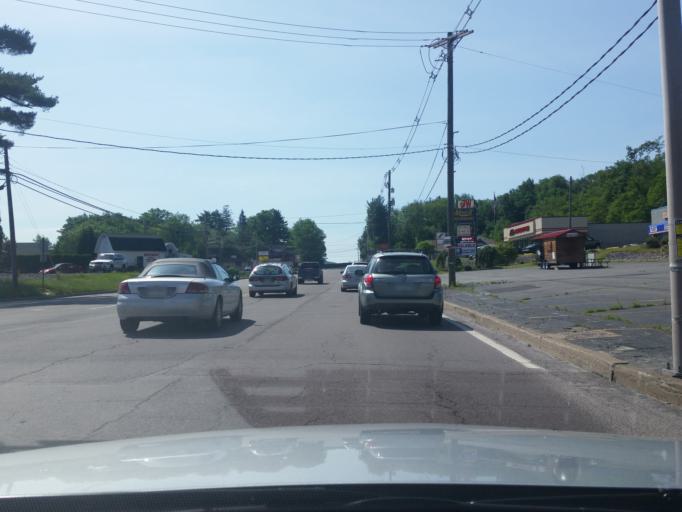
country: US
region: Pennsylvania
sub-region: Luzerne County
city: Shavertown
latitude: 41.3288
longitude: -75.9479
